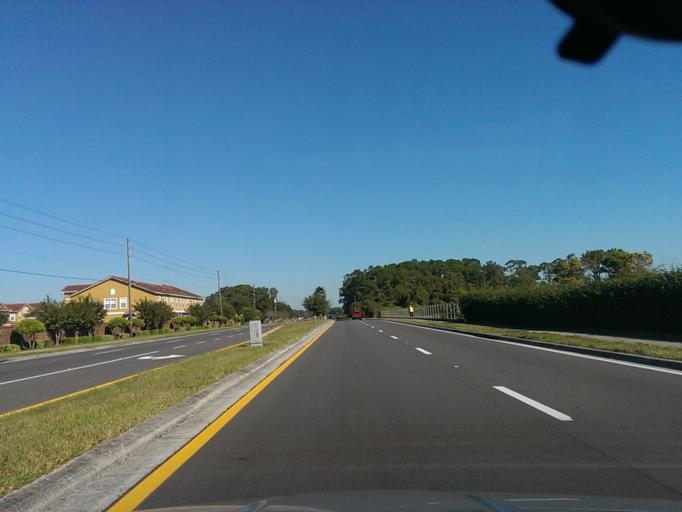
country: US
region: Florida
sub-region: Orange County
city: Doctor Phillips
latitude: 28.4187
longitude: -81.5327
